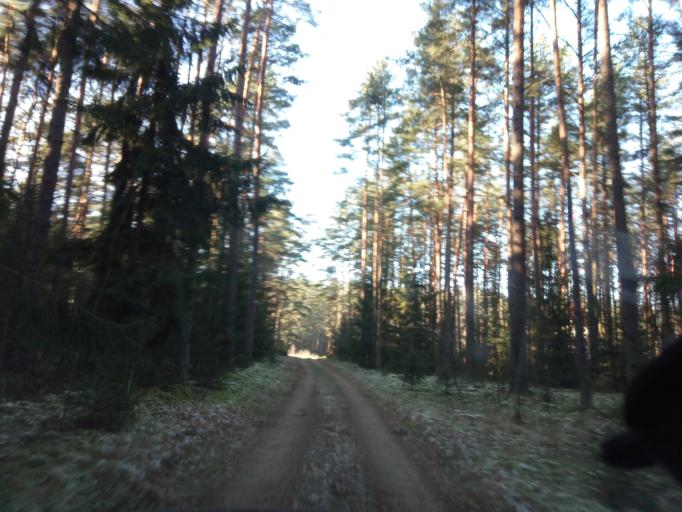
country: LT
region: Alytaus apskritis
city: Druskininkai
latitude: 53.9542
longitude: 23.8632
